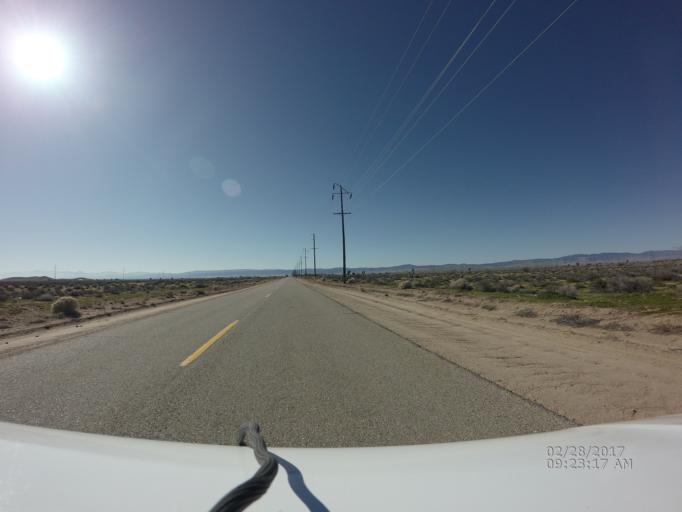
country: US
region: California
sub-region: Kern County
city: Rosamond
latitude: 34.8169
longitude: -118.3261
